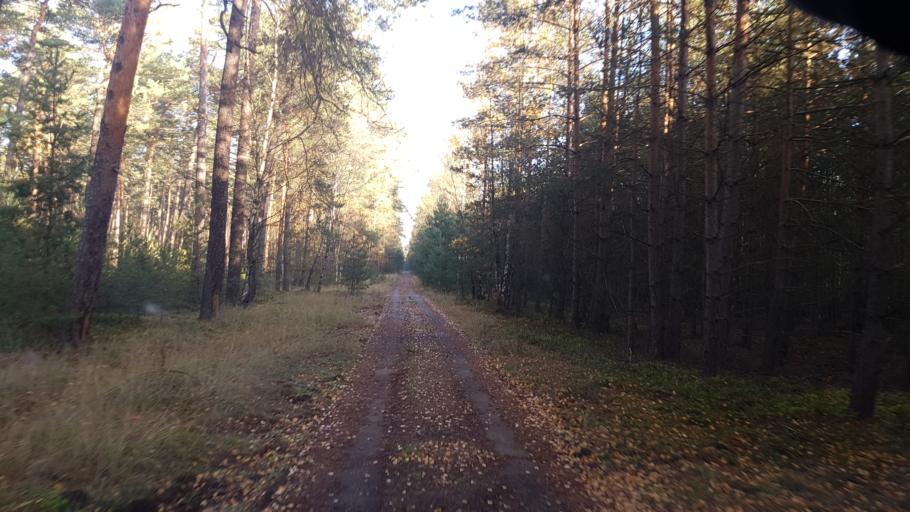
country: DE
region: Brandenburg
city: Crinitz
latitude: 51.7197
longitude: 13.7444
